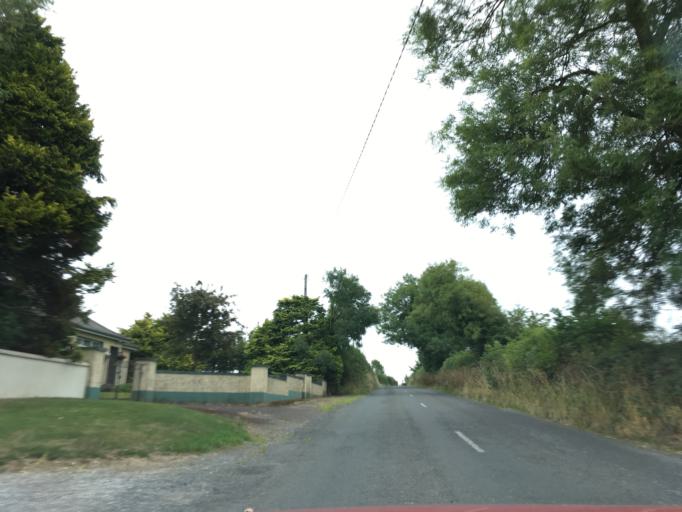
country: IE
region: Munster
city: Cashel
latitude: 52.4741
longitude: -7.8643
